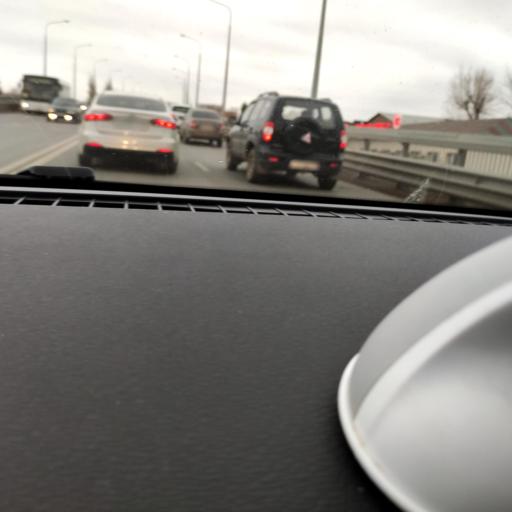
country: RU
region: Samara
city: Samara
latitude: 53.1728
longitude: 50.1946
